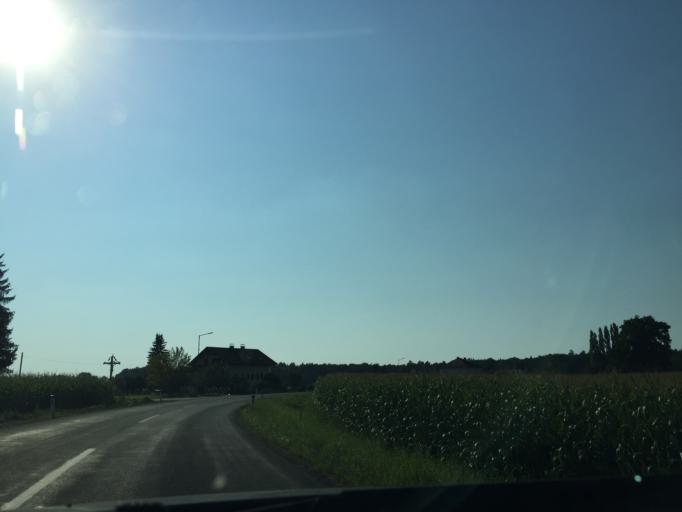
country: AT
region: Styria
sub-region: Politischer Bezirk Suedoststeiermark
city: Deutsch Goritz
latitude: 46.7416
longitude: 15.8388
